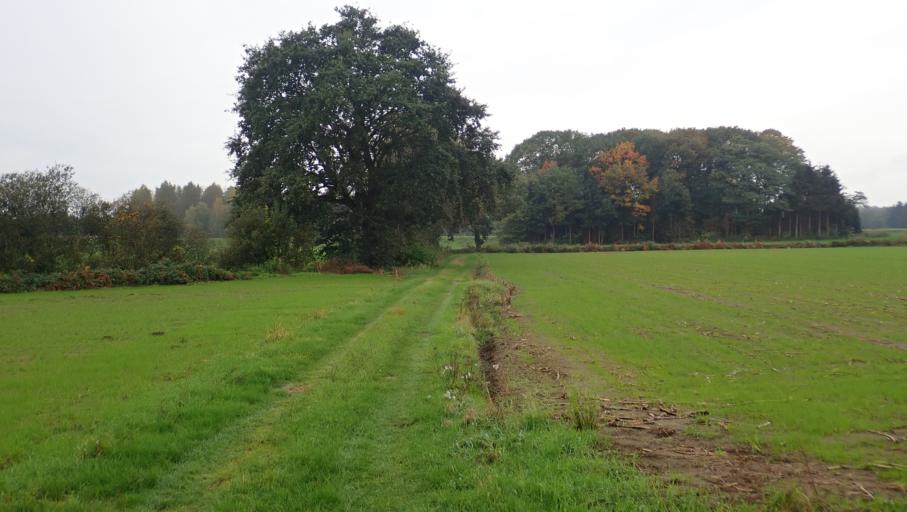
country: BE
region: Flanders
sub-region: Provincie Antwerpen
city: Berlaar
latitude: 51.1368
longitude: 4.6706
